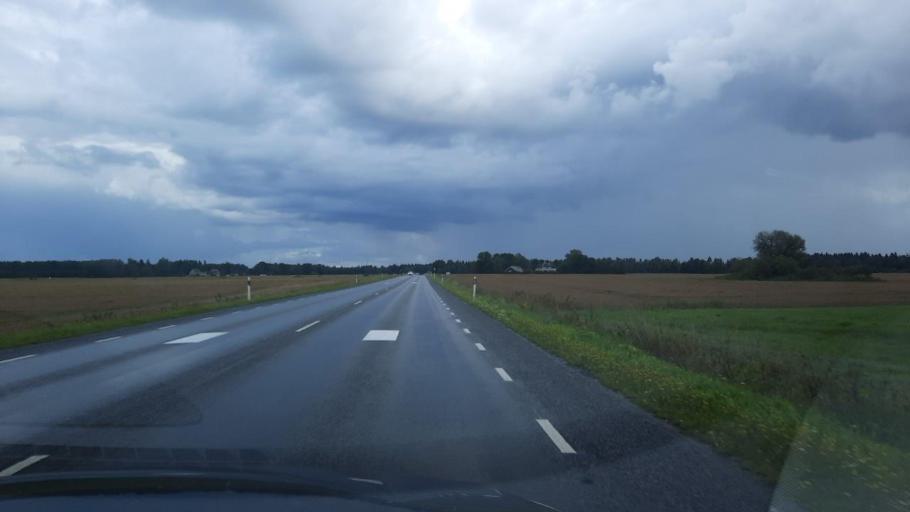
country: EE
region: Jaervamaa
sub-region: Tueri vald
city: Sarevere
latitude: 58.7746
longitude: 25.5134
